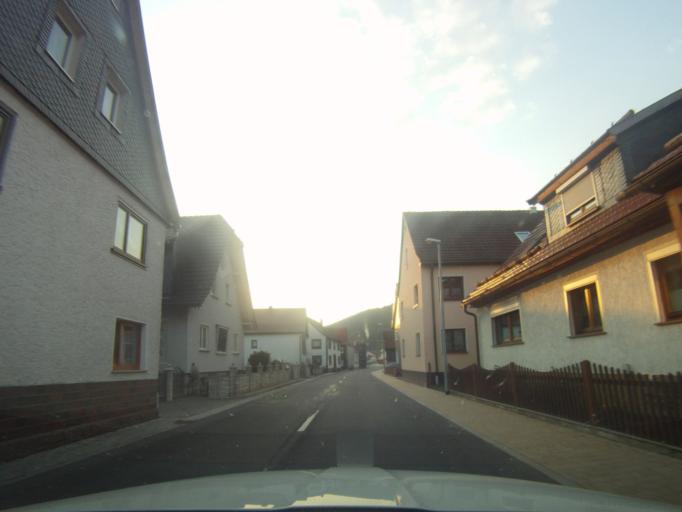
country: DE
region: Thuringia
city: Eisfeld
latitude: 50.4918
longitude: 10.8655
